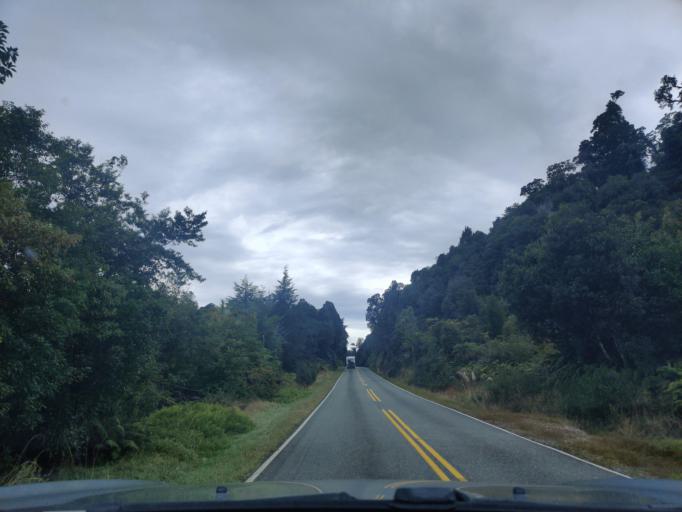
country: NZ
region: West Coast
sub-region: Westland District
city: Hokitika
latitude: -43.0314
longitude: 170.6549
